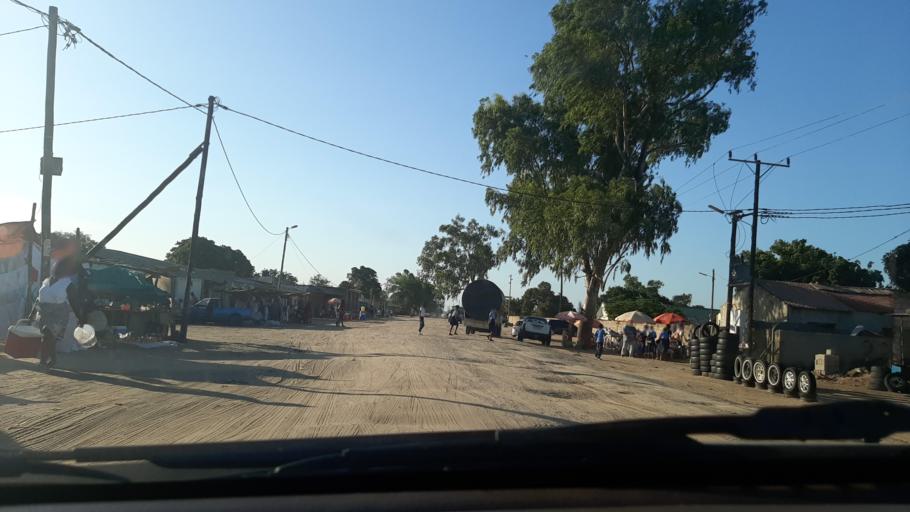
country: MZ
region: Maputo City
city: Maputo
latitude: -25.7365
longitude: 32.5384
